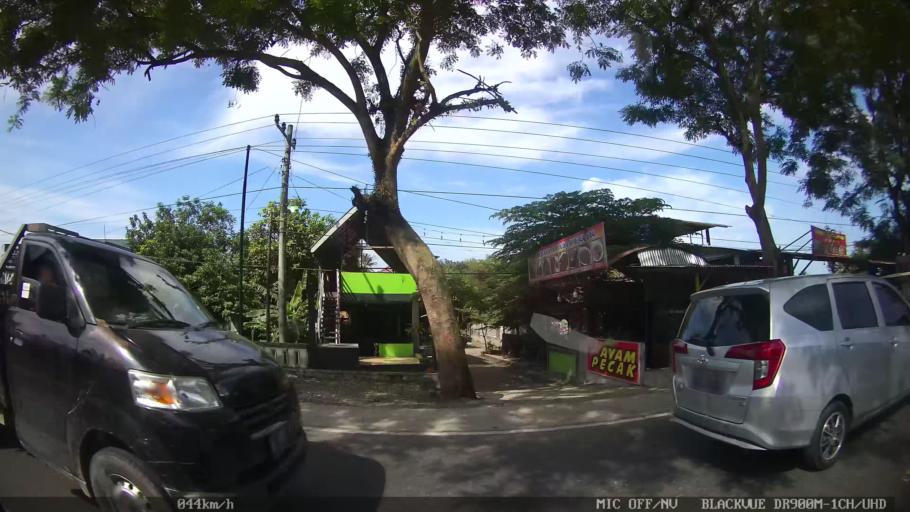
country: ID
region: North Sumatra
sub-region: Kabupaten Langkat
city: Stabat
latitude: 3.7127
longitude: 98.5045
